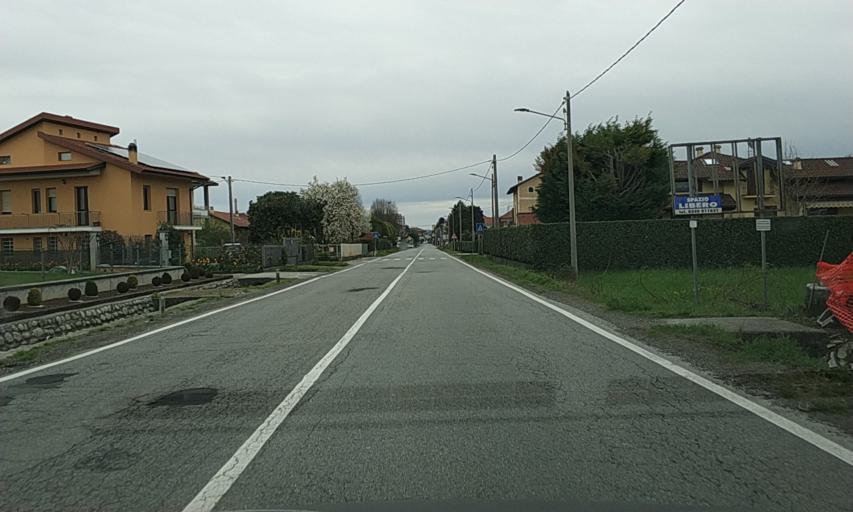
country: IT
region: Piedmont
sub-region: Provincia di Torino
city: Rivarolo Canavese
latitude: 45.3313
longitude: 7.7074
